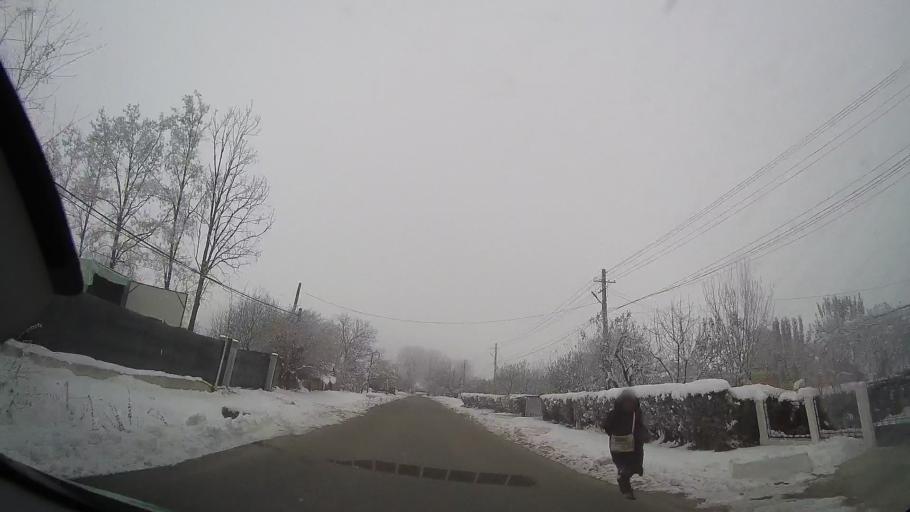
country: RO
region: Neamt
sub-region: Comuna Icusesti
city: Balusesti
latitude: 46.8612
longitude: 27.0150
